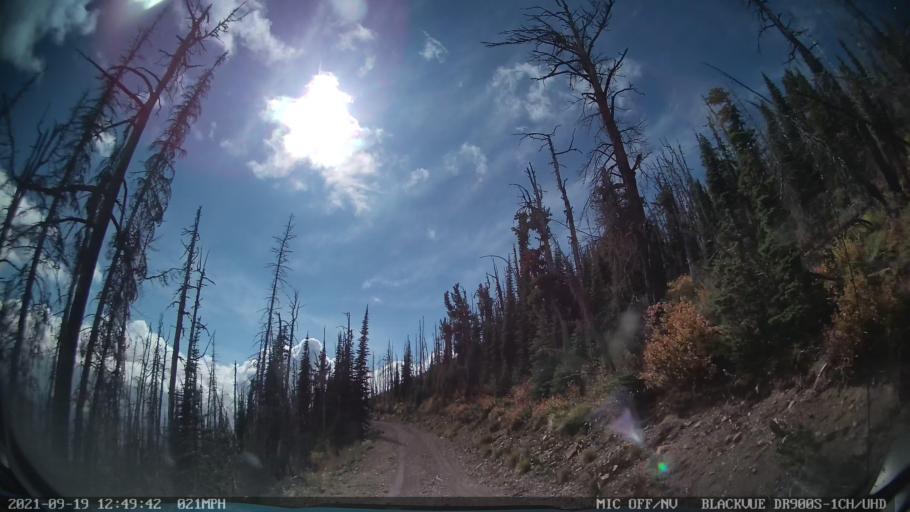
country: US
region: Montana
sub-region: Missoula County
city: Seeley Lake
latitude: 47.1869
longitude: -113.3546
